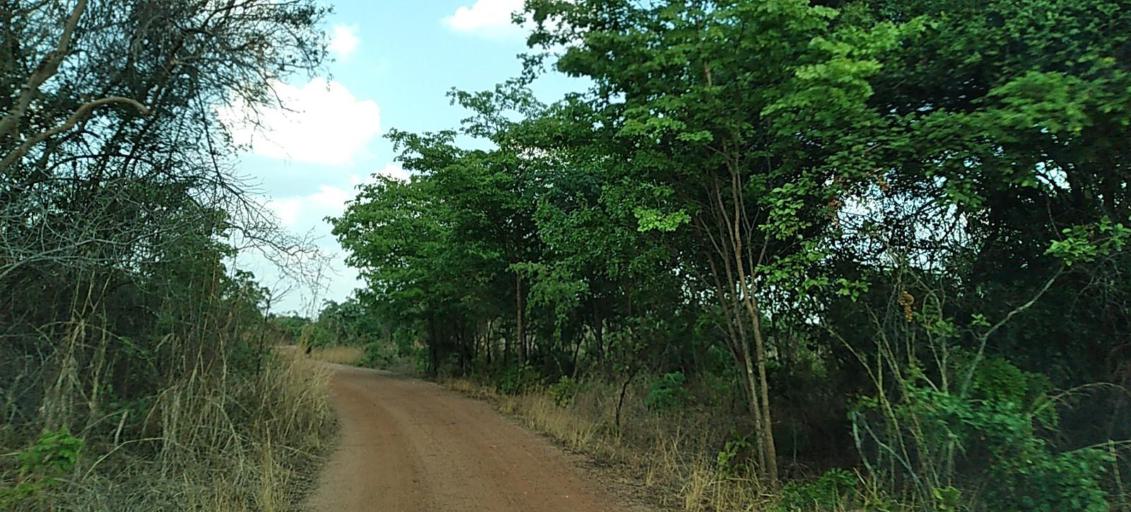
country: ZM
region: Copperbelt
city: Luanshya
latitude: -13.1560
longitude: 28.3256
